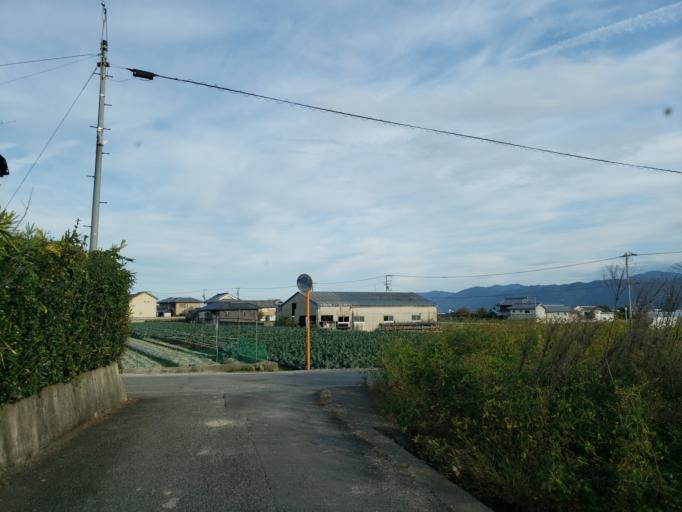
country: JP
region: Tokushima
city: Wakimachi
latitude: 34.0930
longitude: 134.2251
